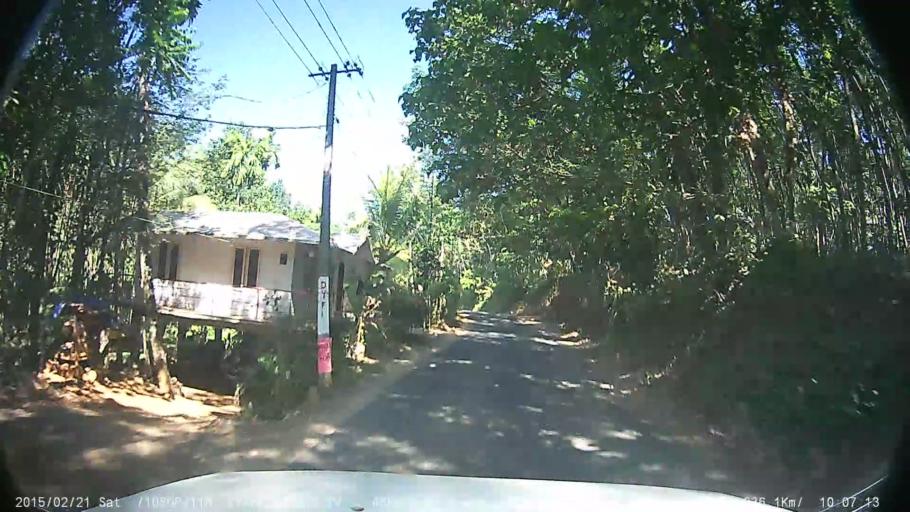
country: IN
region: Kerala
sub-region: Ernakulam
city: Piravam
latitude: 9.8710
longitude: 76.6076
